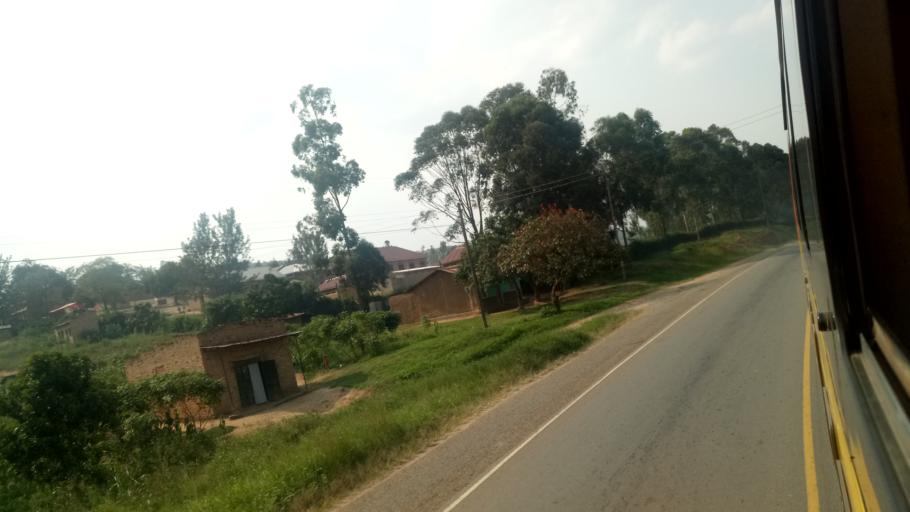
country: UG
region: Western Region
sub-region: Mbarara District
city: Mbarara
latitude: -0.5336
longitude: 30.7164
